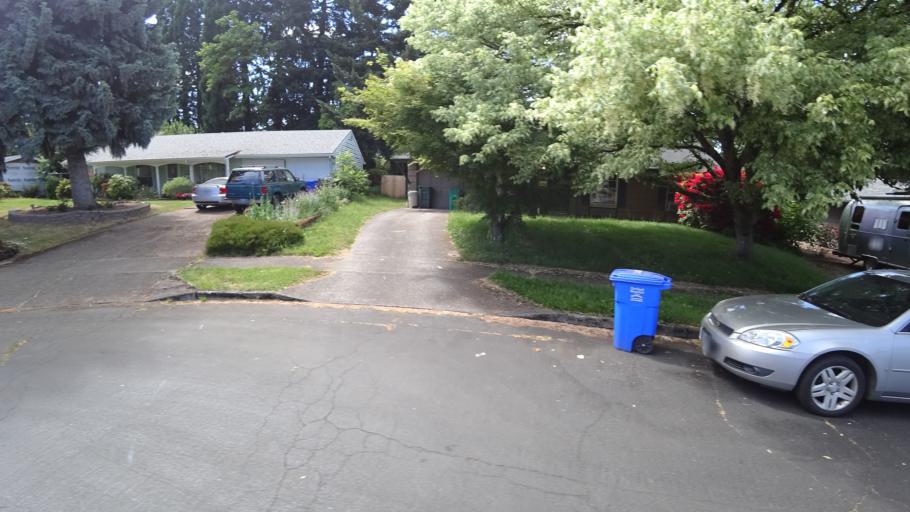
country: US
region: Oregon
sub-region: Washington County
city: West Haven
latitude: 45.5887
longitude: -122.7312
